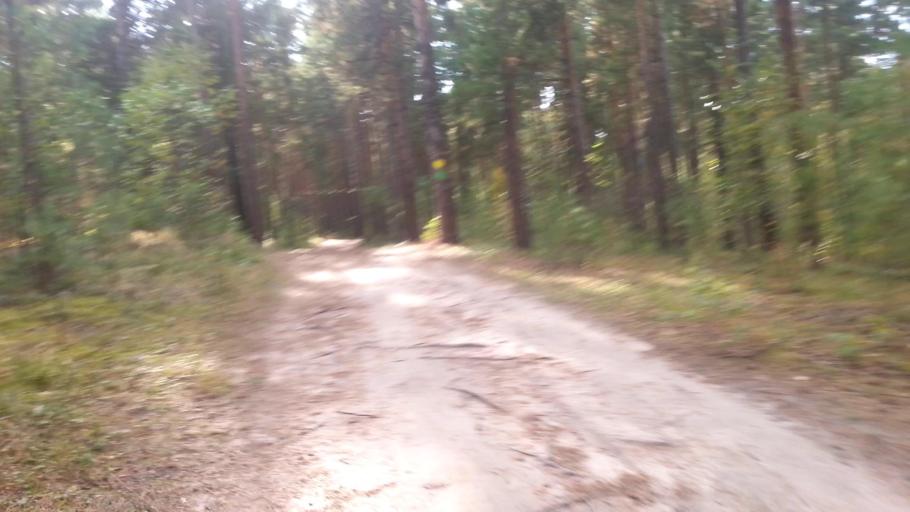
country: RU
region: Altai Krai
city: Yuzhnyy
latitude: 53.2854
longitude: 83.7000
